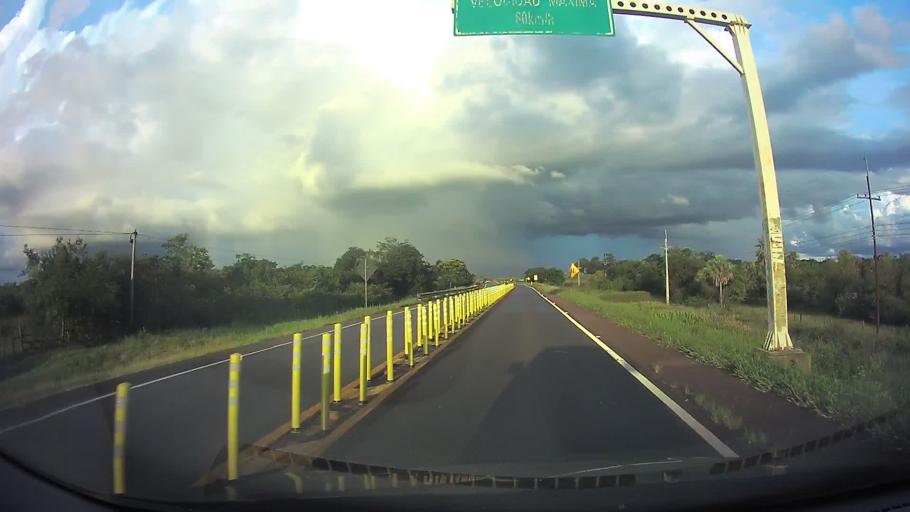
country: PY
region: Paraguari
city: Carapegua
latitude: -25.7506
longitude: -57.2198
